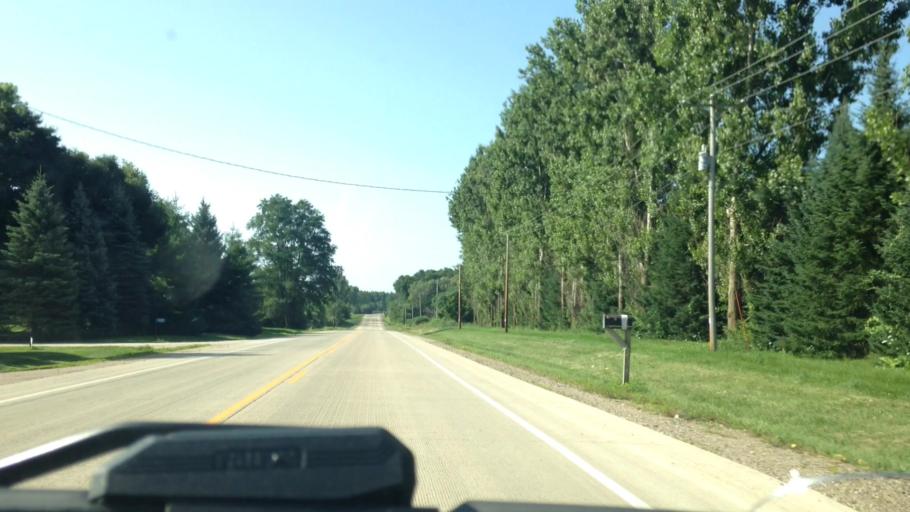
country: US
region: Wisconsin
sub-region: Dodge County
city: Mayville
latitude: 43.4638
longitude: -88.5614
